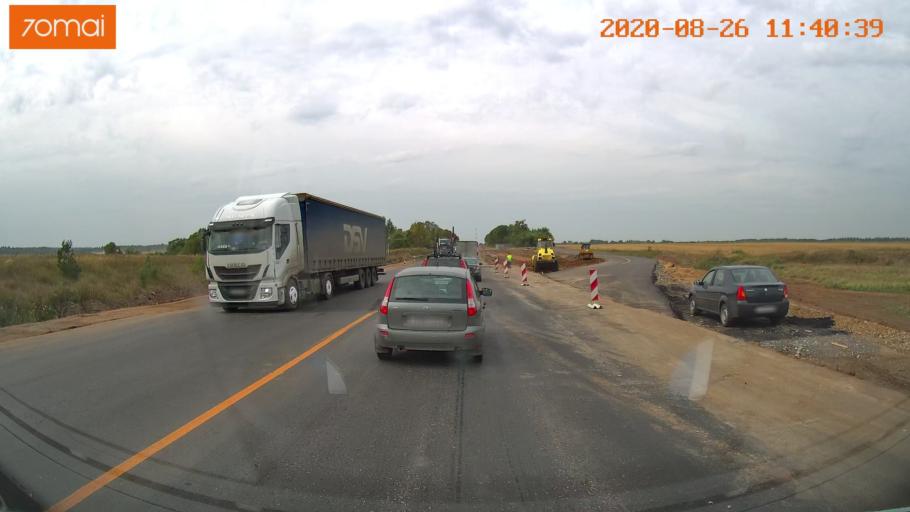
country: RU
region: Rjazan
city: Shilovo
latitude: 54.2948
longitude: 40.7214
